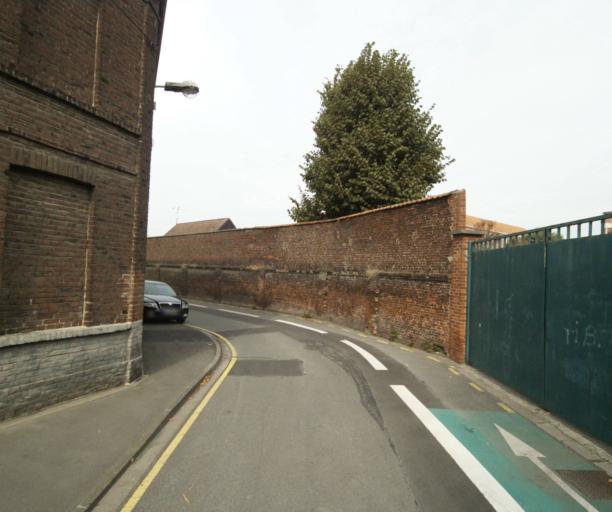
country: FR
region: Nord-Pas-de-Calais
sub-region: Departement du Nord
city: Hallennes-lez-Haubourdin
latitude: 50.6108
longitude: 2.9758
